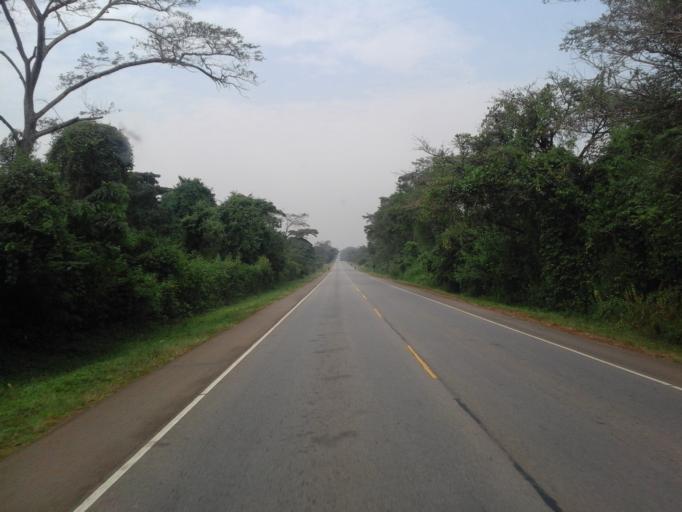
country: UG
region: Eastern Region
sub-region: Busia District
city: Busia
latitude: 0.5291
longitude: 33.9793
